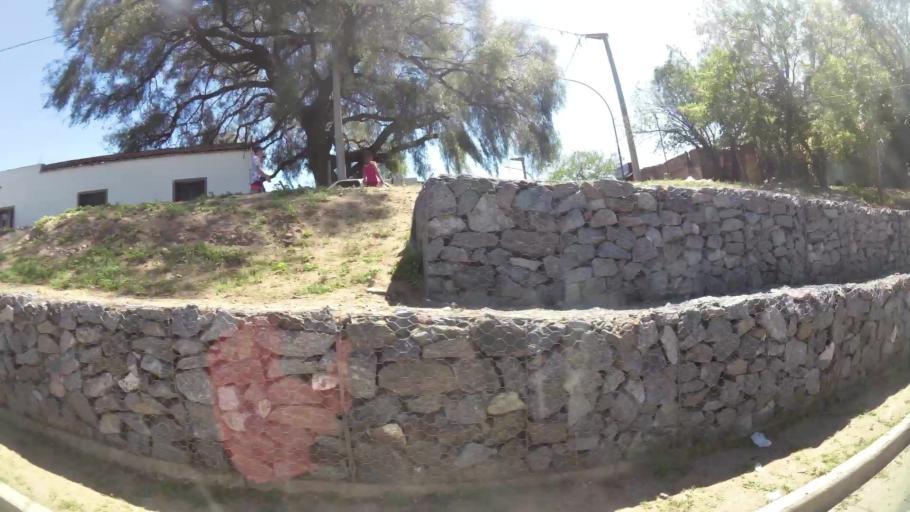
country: AR
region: Cordoba
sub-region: Departamento de Capital
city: Cordoba
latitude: -31.4099
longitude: -64.1379
